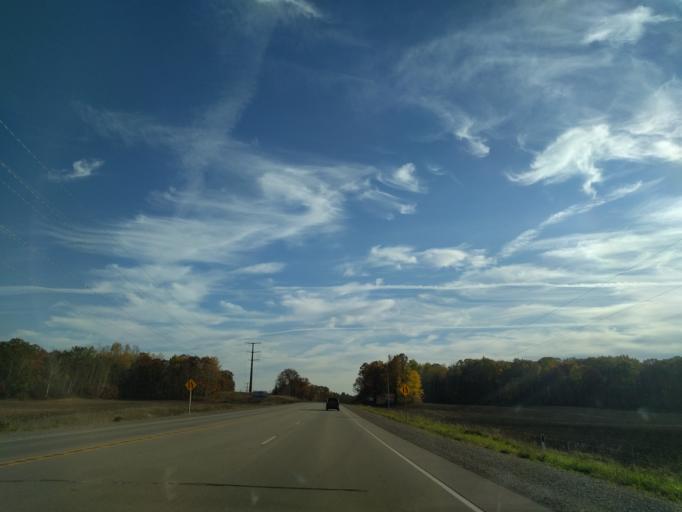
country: US
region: Wisconsin
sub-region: Marinette County
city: Peshtigo
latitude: 45.2640
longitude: -87.9905
